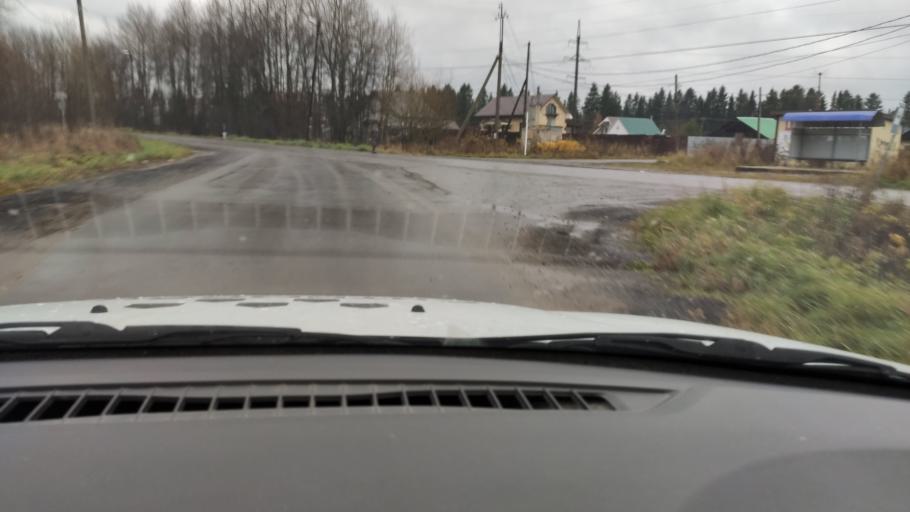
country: RU
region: Perm
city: Sylva
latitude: 58.0353
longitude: 56.7398
